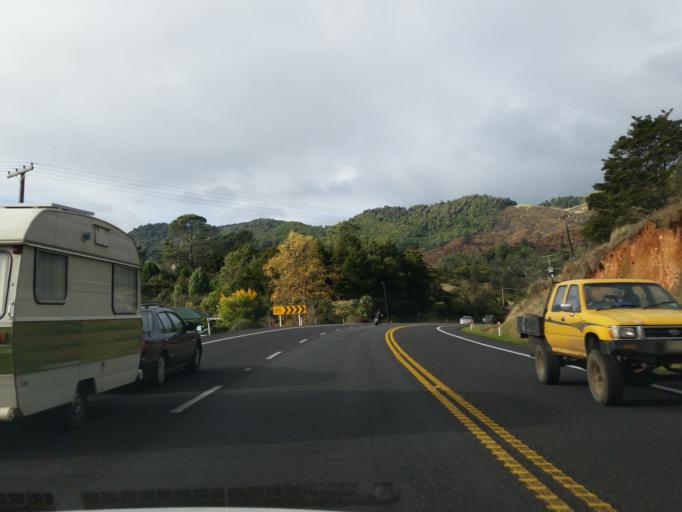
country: NZ
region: Waikato
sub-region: Hauraki District
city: Paeroa
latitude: -37.4021
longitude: 175.7035
